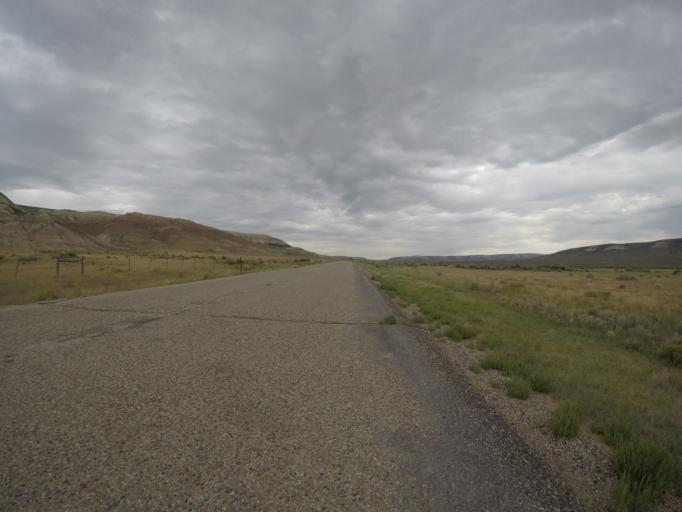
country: US
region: Wyoming
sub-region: Lincoln County
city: Kemmerer
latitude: 41.8230
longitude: -110.7517
